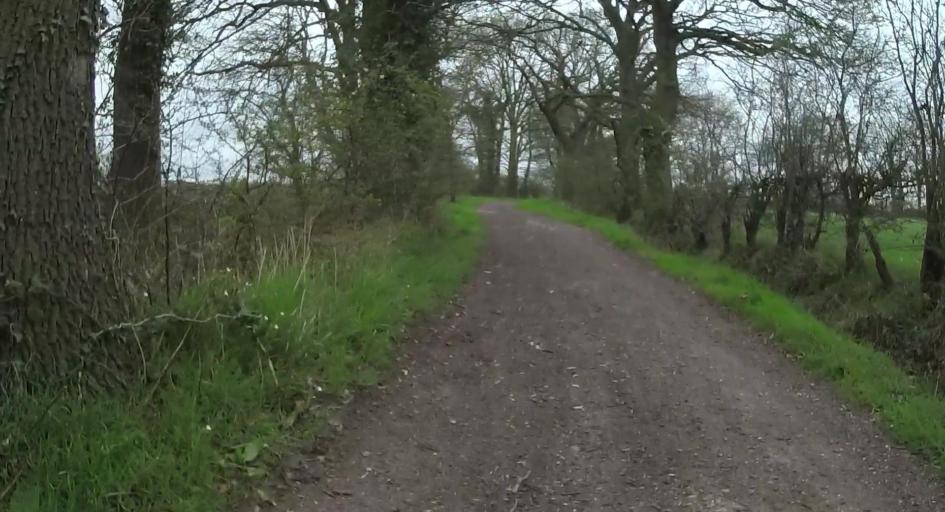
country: GB
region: England
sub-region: West Berkshire
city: Arborfield
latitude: 51.4097
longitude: -0.9085
